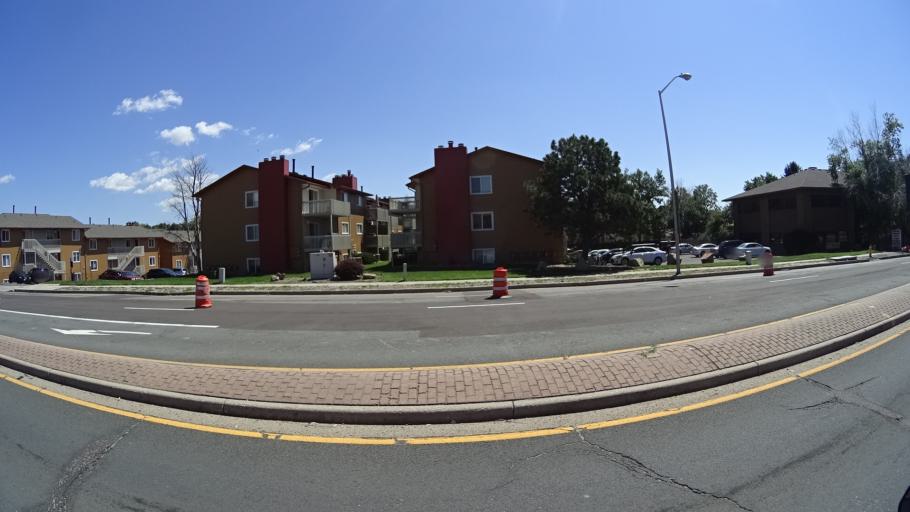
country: US
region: Colorado
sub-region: El Paso County
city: Colorado Springs
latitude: 38.9125
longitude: -104.7747
